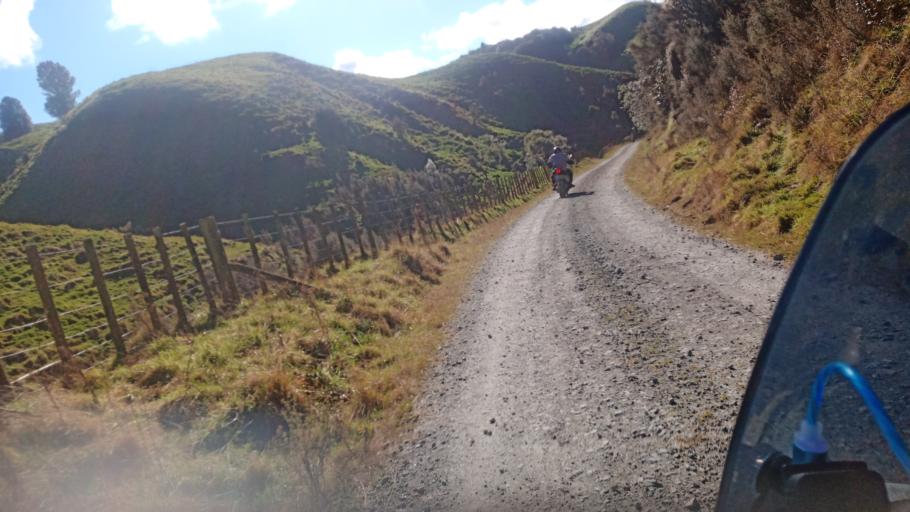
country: NZ
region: Hawke's Bay
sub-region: Wairoa District
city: Wairoa
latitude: -38.6636
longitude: 177.4864
